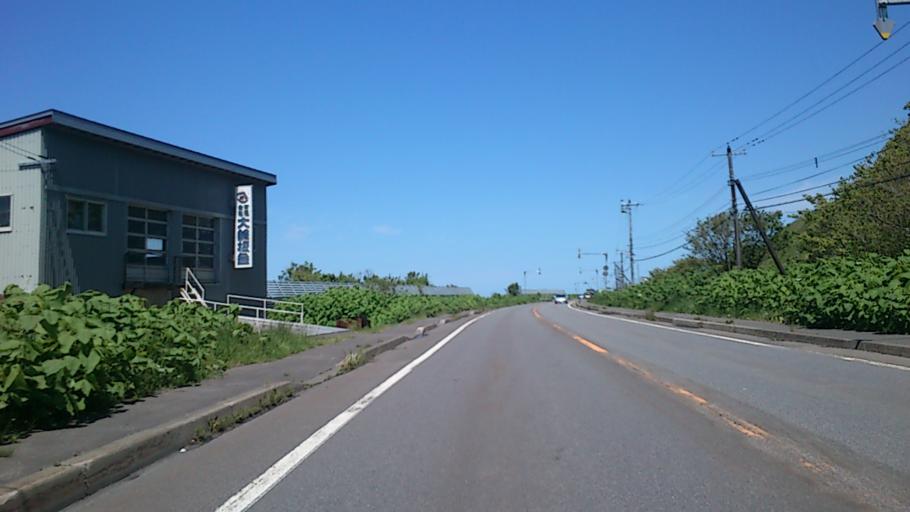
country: JP
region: Hokkaido
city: Rumoi
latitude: 43.9722
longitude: 141.6467
